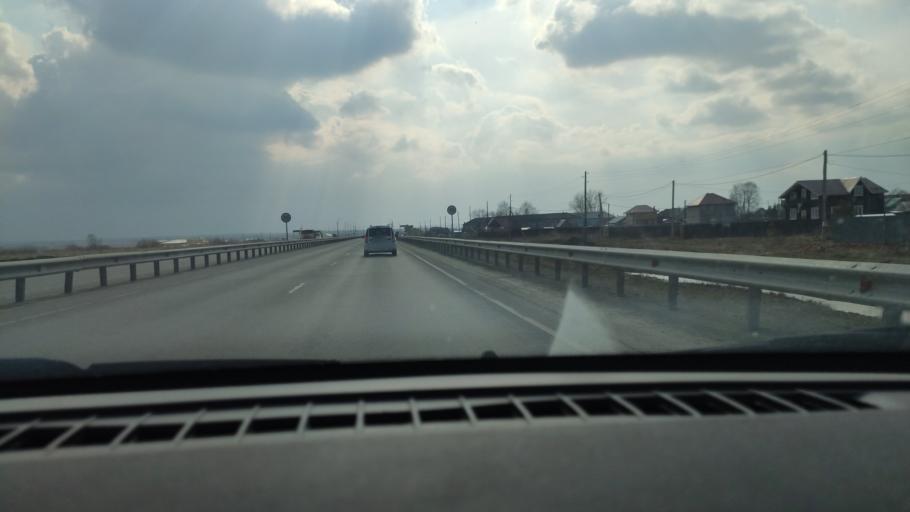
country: RU
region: Perm
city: Kultayevo
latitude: 57.9114
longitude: 55.9944
